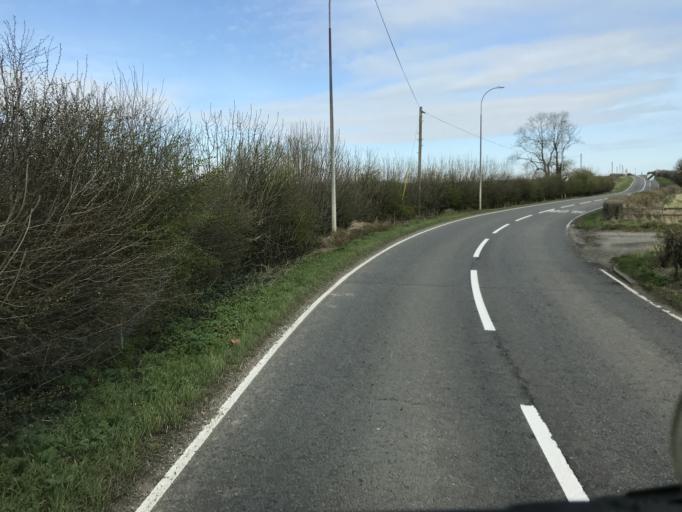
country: GB
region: England
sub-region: Lincolnshire
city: Market Rasen
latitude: 53.3907
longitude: -0.4050
